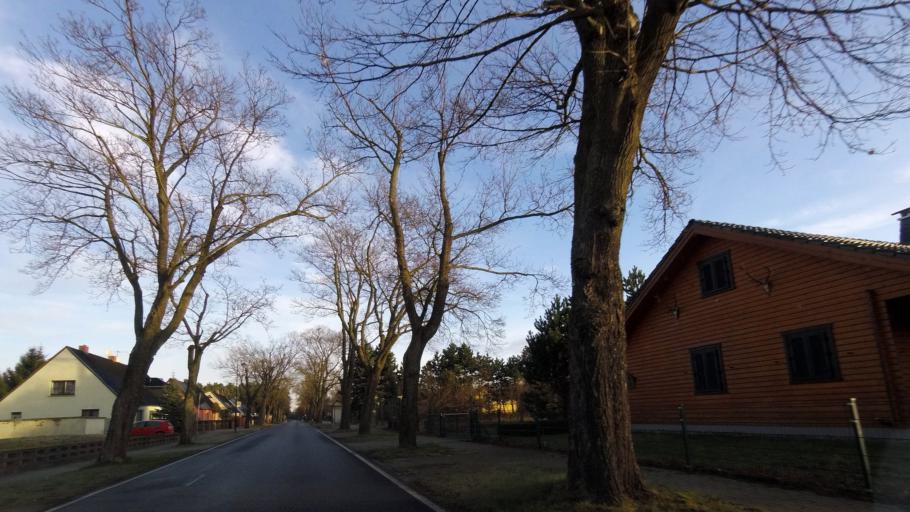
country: DE
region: Brandenburg
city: Niedergorsdorf
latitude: 52.0123
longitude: 12.9416
